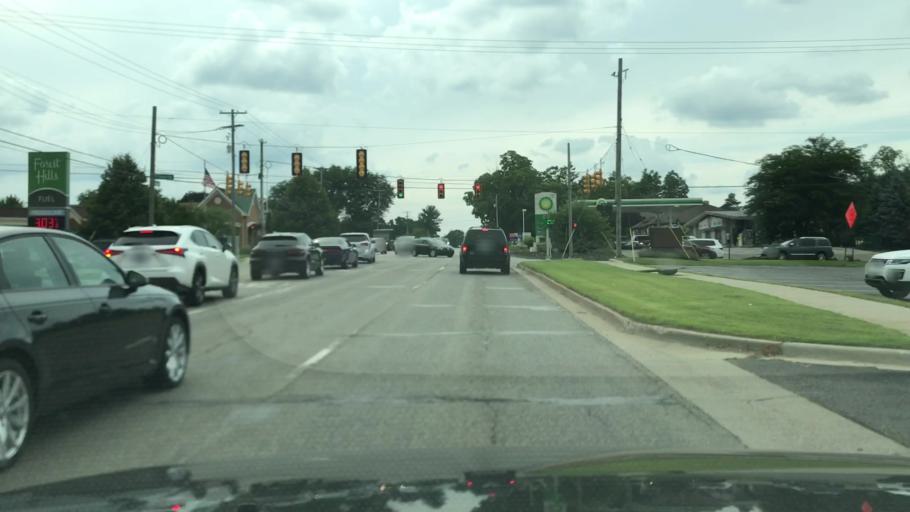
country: US
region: Michigan
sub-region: Kent County
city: East Grand Rapids
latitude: 42.9462
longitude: -85.5551
